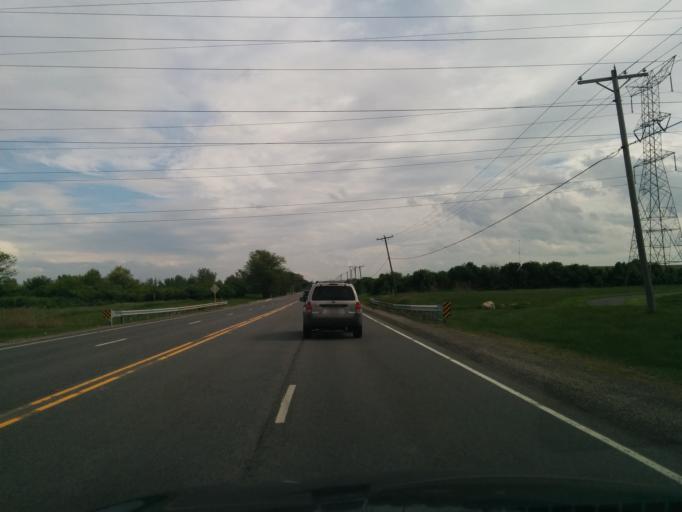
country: US
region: Illinois
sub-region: Will County
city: Romeoville
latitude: 41.6326
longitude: -88.0805
